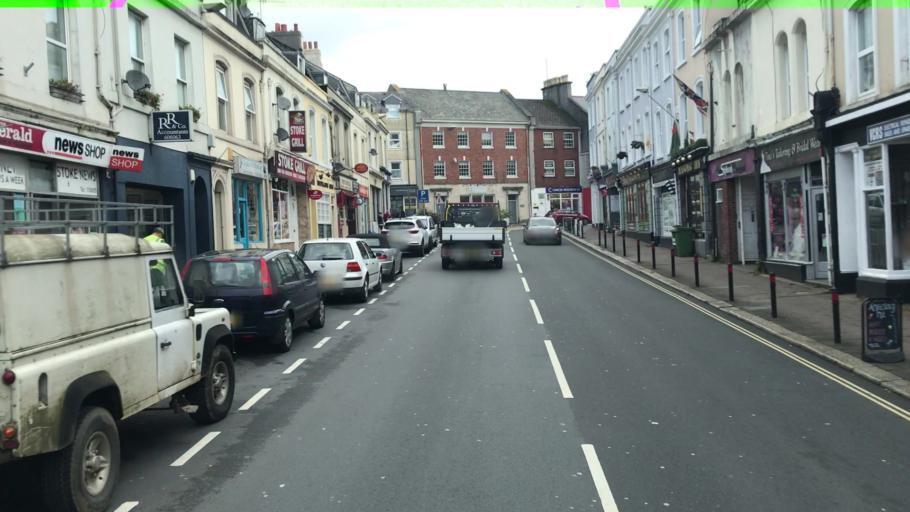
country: GB
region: England
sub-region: Cornwall
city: Millbrook
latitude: 50.3804
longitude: -4.1666
